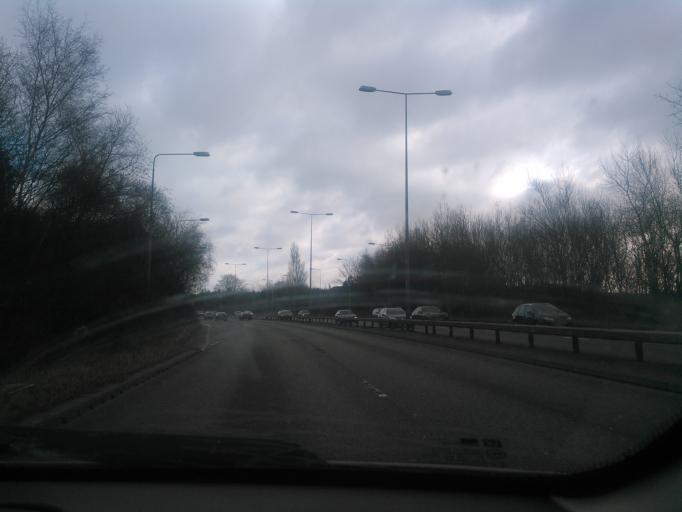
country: GB
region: England
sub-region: Staffordshire
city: Longton
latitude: 52.9827
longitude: -2.1269
